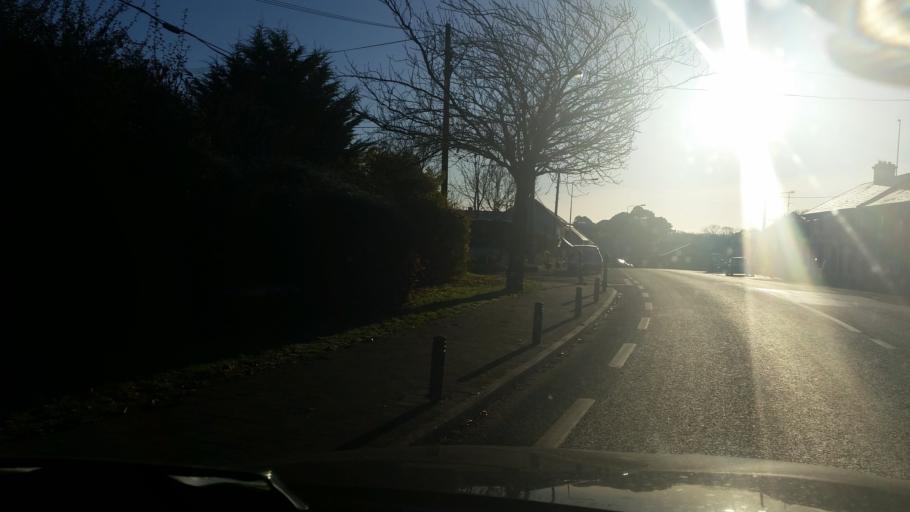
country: IE
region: Leinster
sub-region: Loch Garman
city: Gorey
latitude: 52.6105
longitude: -6.3053
